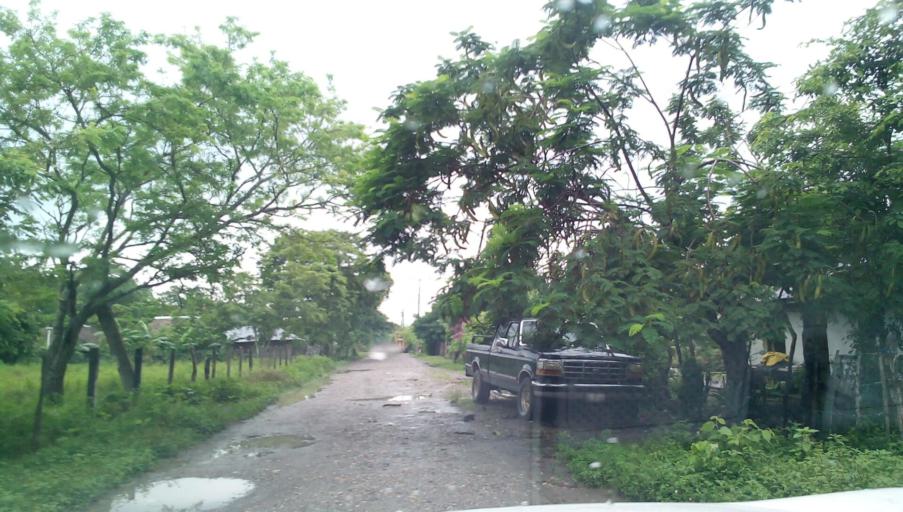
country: MX
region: Veracruz
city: Tempoal de Sanchez
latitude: 21.4176
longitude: -98.4290
